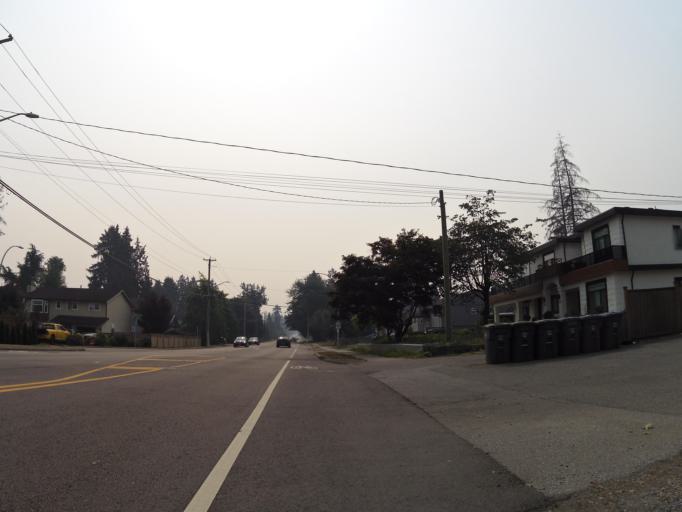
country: CA
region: British Columbia
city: Surrey
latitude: 49.1262
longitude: -122.8567
